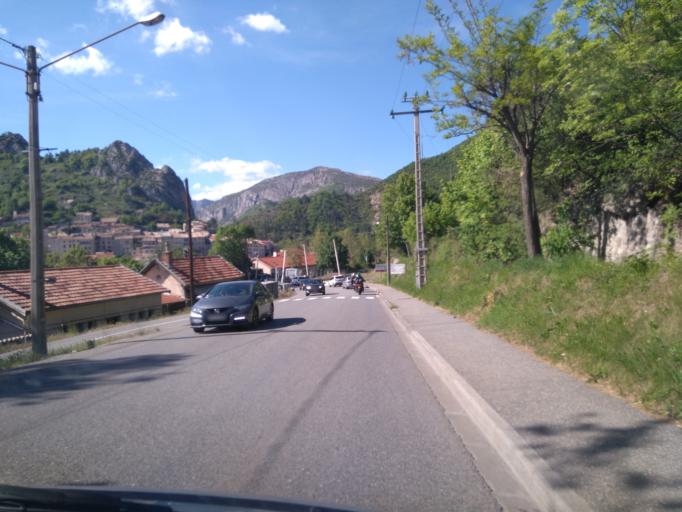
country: FR
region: Provence-Alpes-Cote d'Azur
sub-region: Departement des Hautes-Alpes
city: Serres
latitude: 44.4258
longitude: 5.7186
